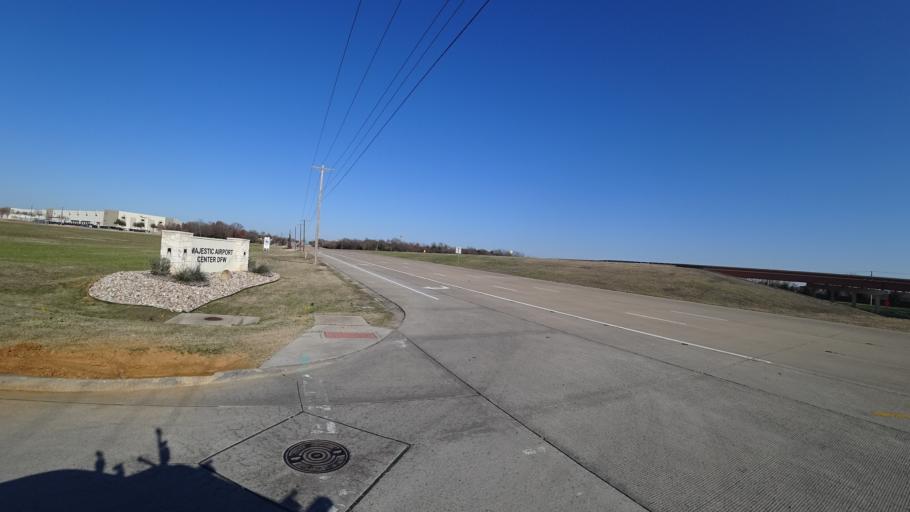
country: US
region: Texas
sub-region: Dallas County
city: Coppell
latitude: 32.9910
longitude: -97.0088
